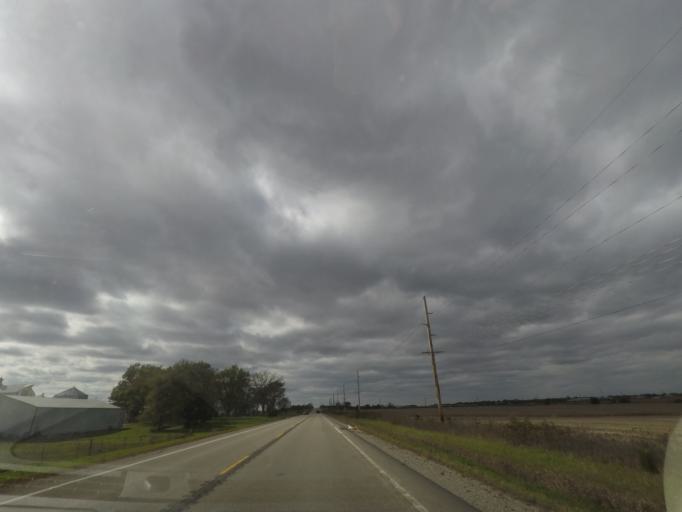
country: US
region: Iowa
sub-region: Story County
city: Huxley
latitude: 41.8778
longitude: -93.5613
